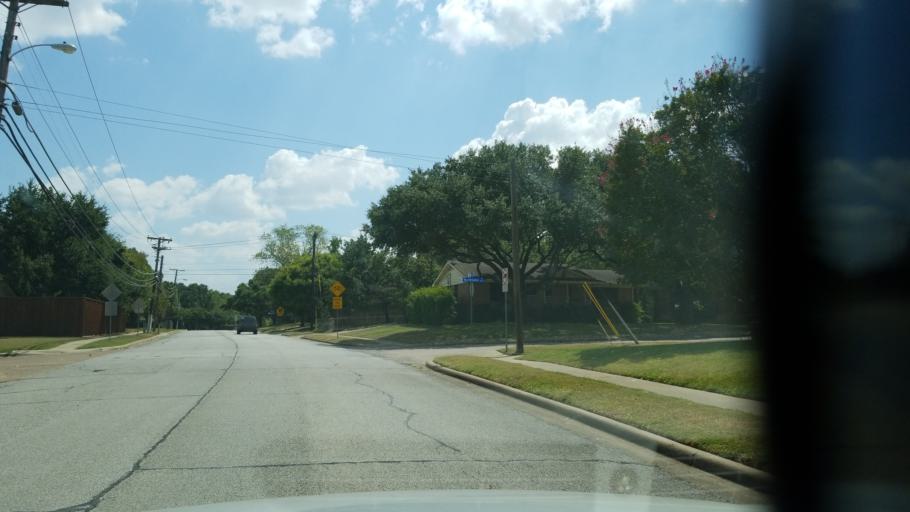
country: US
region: Texas
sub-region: Dallas County
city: Richardson
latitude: 32.9592
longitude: -96.7620
